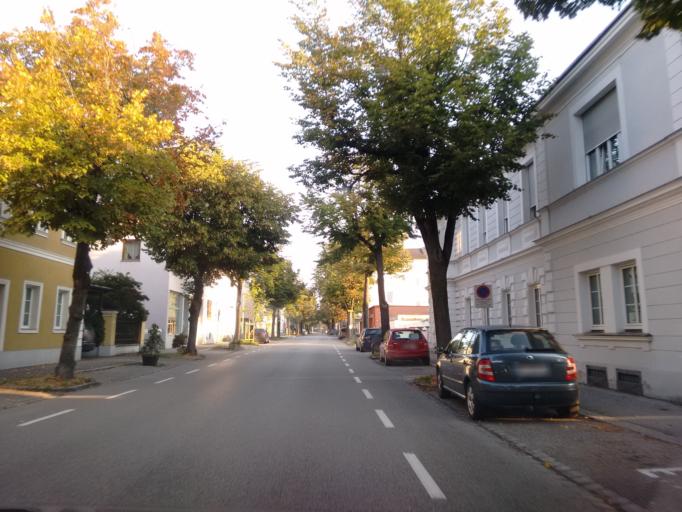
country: AT
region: Upper Austria
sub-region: Wels Stadt
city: Wels
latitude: 48.1674
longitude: 14.0231
